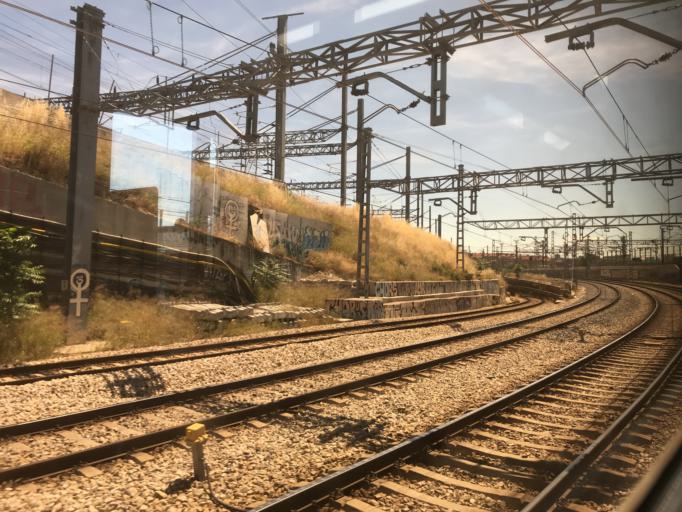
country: ES
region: Madrid
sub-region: Provincia de Madrid
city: Retiro
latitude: 40.4015
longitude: -3.6836
